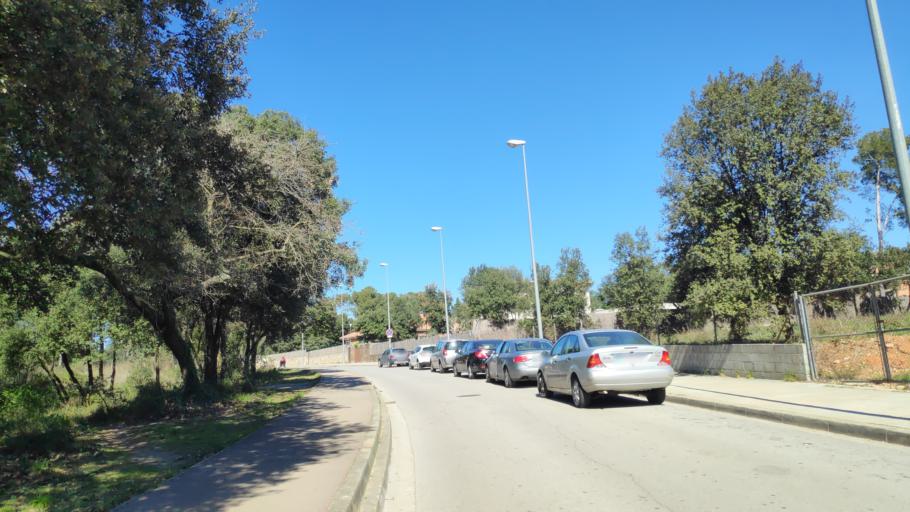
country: ES
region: Catalonia
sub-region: Provincia de Barcelona
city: Sant Quirze del Valles
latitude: 41.5575
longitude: 2.0696
